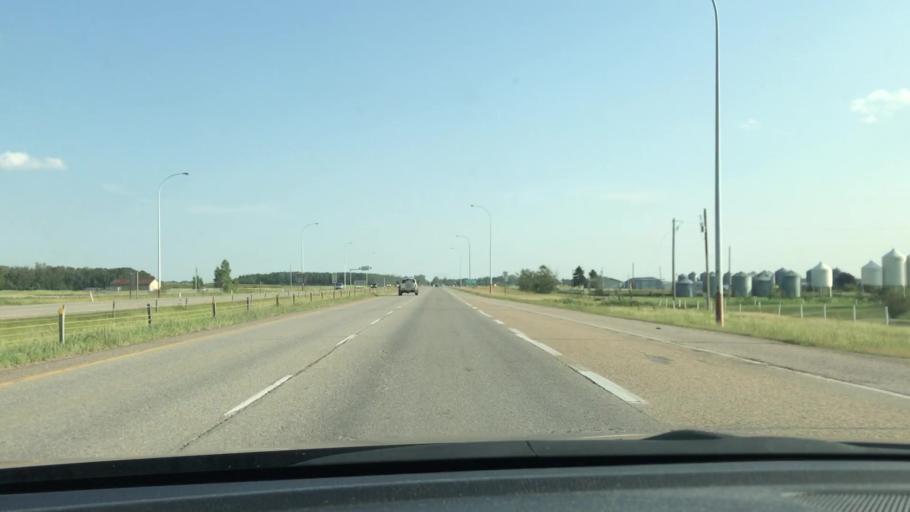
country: CA
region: Alberta
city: Leduc
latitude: 53.2517
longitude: -113.5619
